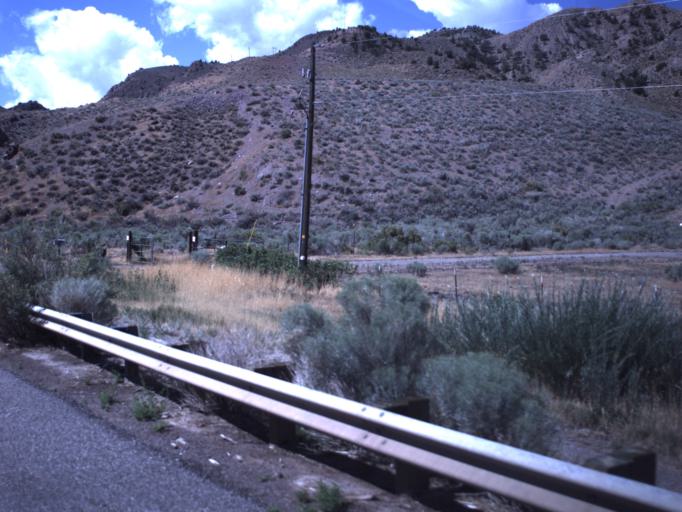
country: US
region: Utah
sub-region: Sevier County
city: Monroe
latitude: 38.5823
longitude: -112.2583
